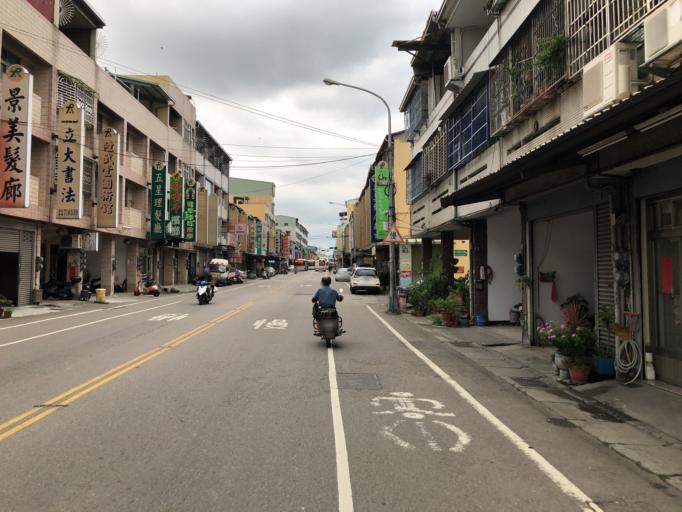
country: TW
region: Taiwan
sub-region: Taichung City
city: Taichung
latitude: 24.1029
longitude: 120.7290
